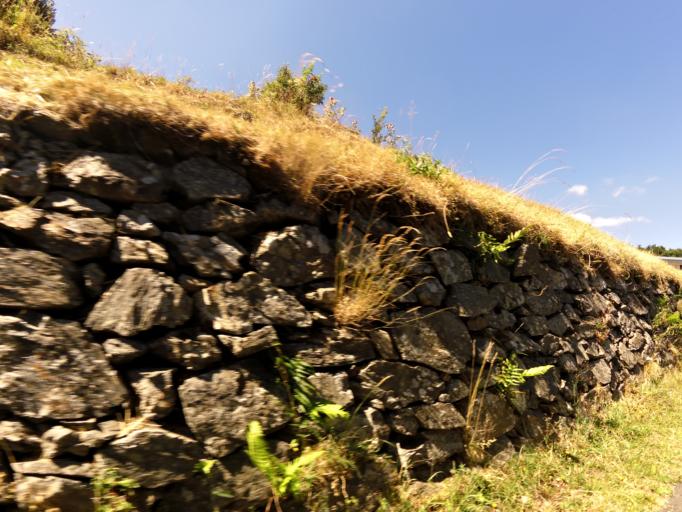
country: FR
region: Languedoc-Roussillon
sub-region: Departement du Gard
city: Valleraugue
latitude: 44.1026
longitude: 3.5419
